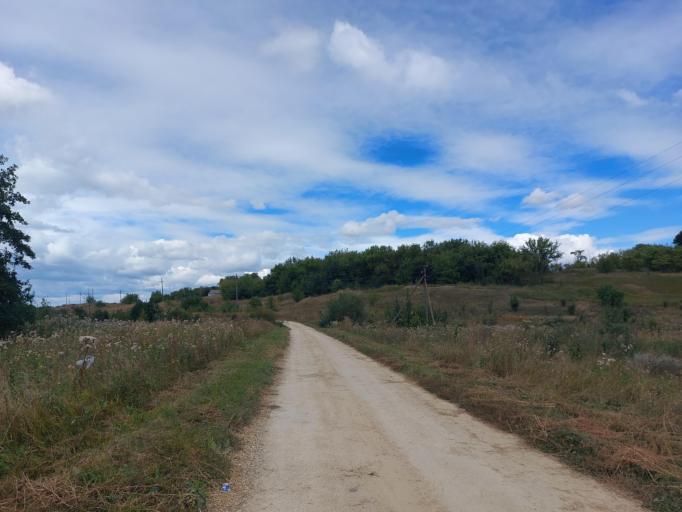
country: RU
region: Lipetsk
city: Terbuny
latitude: 52.2687
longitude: 38.2046
